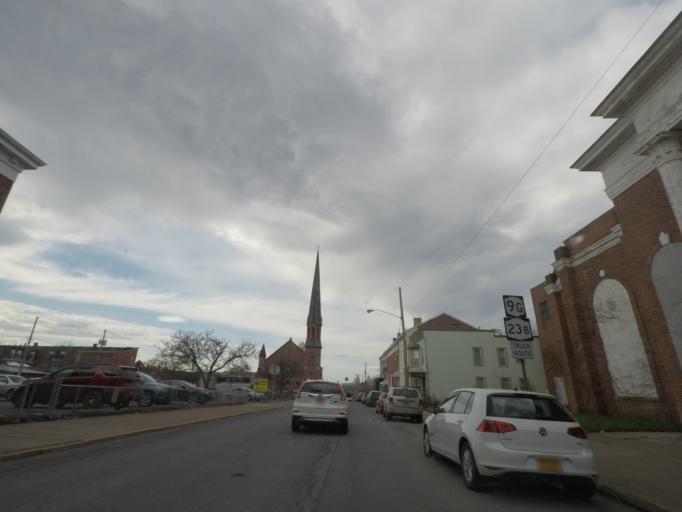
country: US
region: New York
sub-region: Columbia County
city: Oakdale
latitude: 42.2481
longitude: -73.7829
